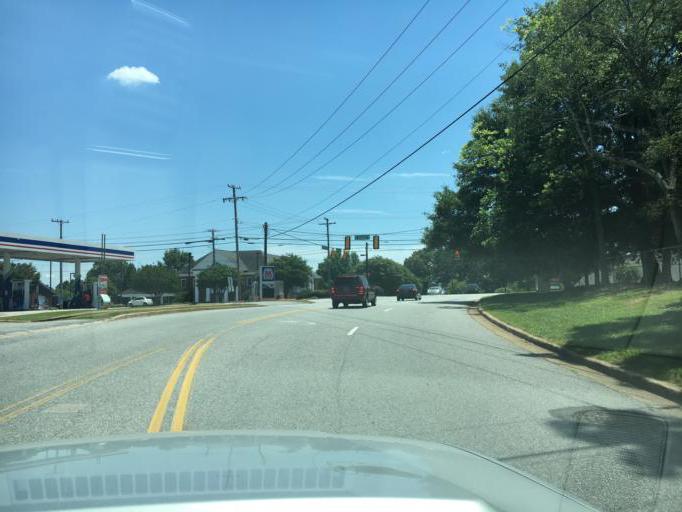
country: US
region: South Carolina
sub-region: Greenville County
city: Greer
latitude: 34.9428
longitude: -82.2483
